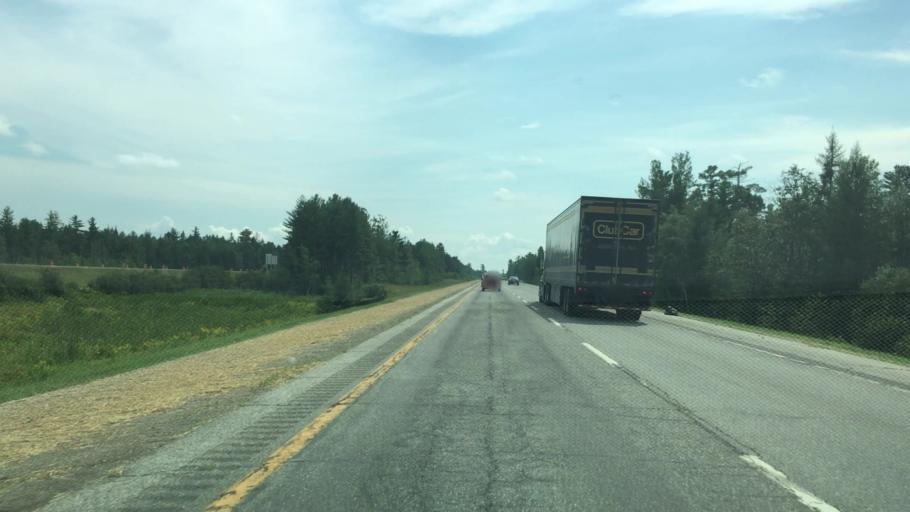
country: US
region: Maine
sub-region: Penobscot County
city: Medway
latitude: 45.5858
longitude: -68.5431
